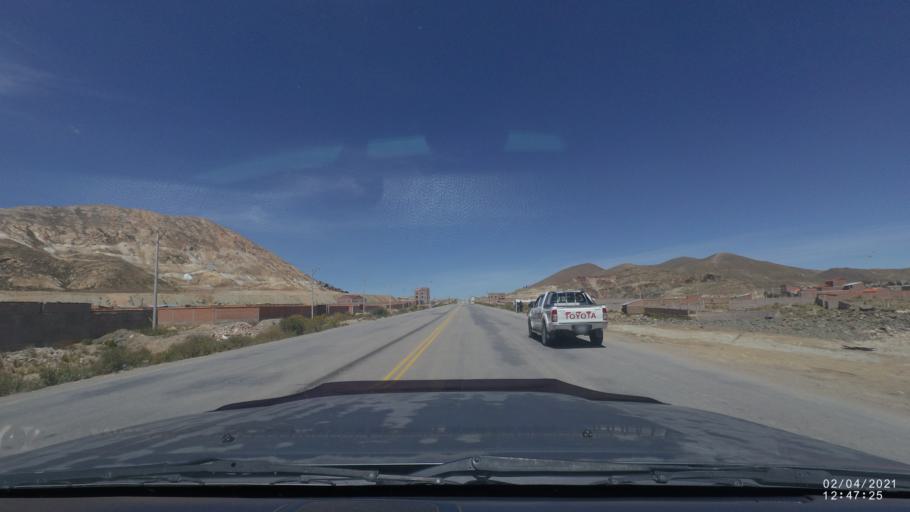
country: BO
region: Oruro
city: Oruro
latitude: -17.9527
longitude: -67.1441
